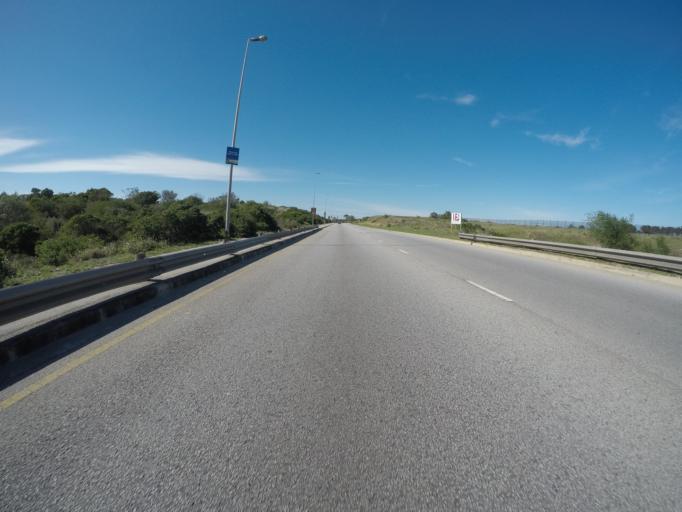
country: ZA
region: Eastern Cape
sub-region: Nelson Mandela Bay Metropolitan Municipality
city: Port Elizabeth
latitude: -33.9857
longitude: 25.6412
